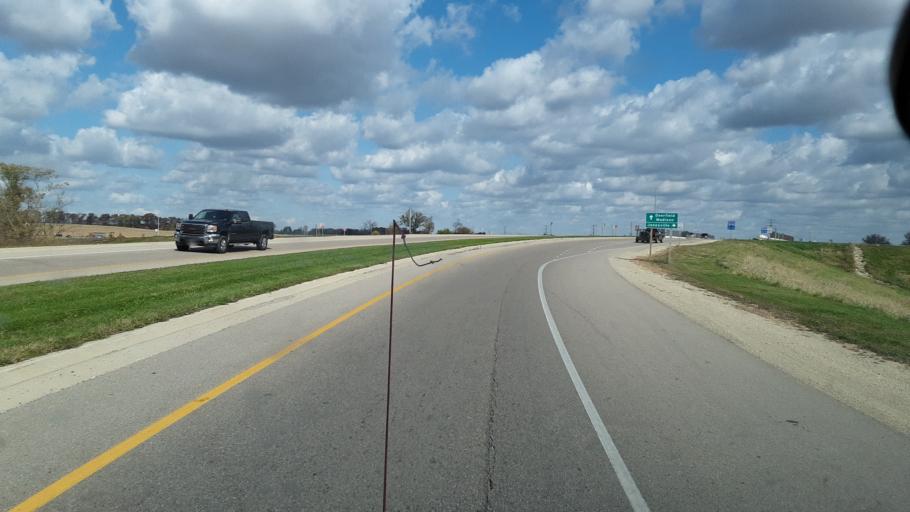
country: US
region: Wisconsin
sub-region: Rock County
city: Edgerton
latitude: 42.8709
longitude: -89.0578
